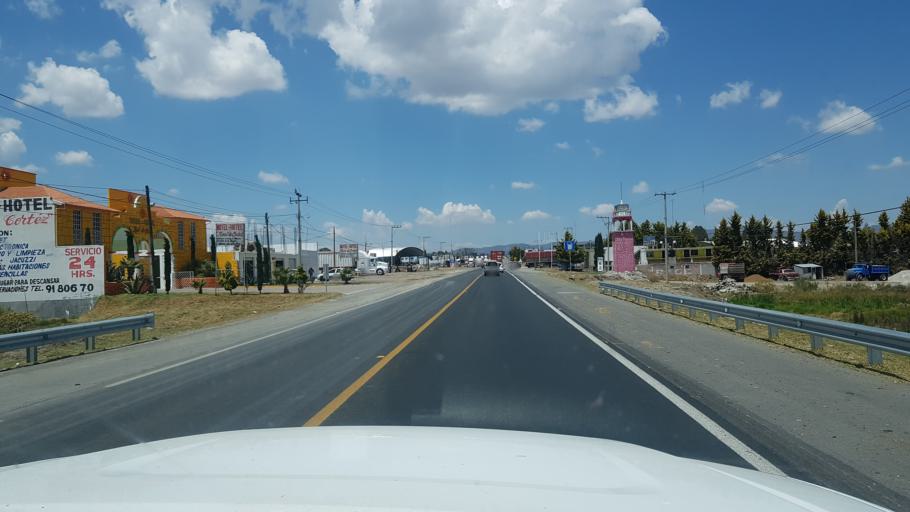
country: MX
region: Hidalgo
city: Calpulalpan
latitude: 19.5846
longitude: -98.5402
